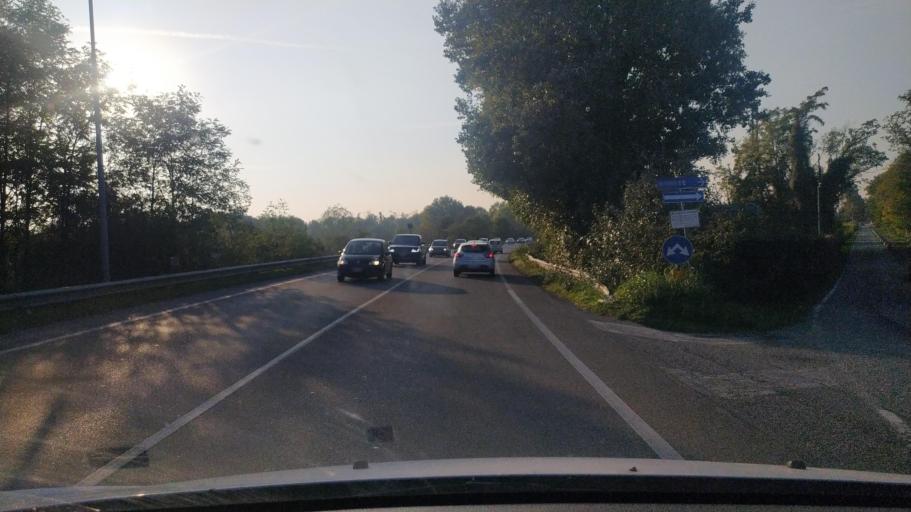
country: IT
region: Lombardy
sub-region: Provincia di Lodi
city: Zelo Buon Persico
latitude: 45.4033
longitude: 9.4562
